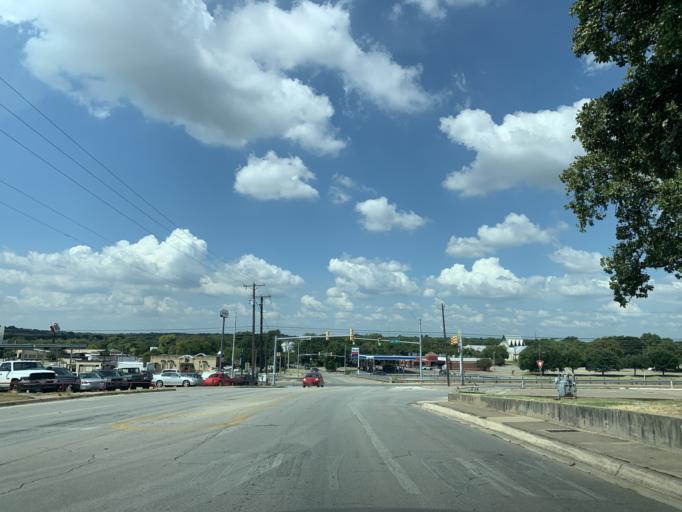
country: US
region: Texas
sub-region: Tarrant County
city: Azle
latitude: 32.8924
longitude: -97.5394
